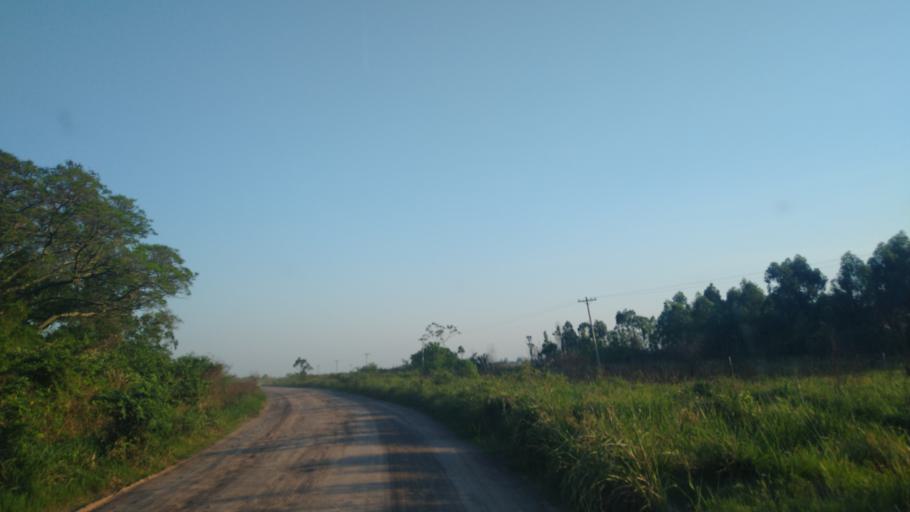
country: PY
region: Neembucu
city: Cerrito
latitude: -27.3962
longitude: -57.6583
